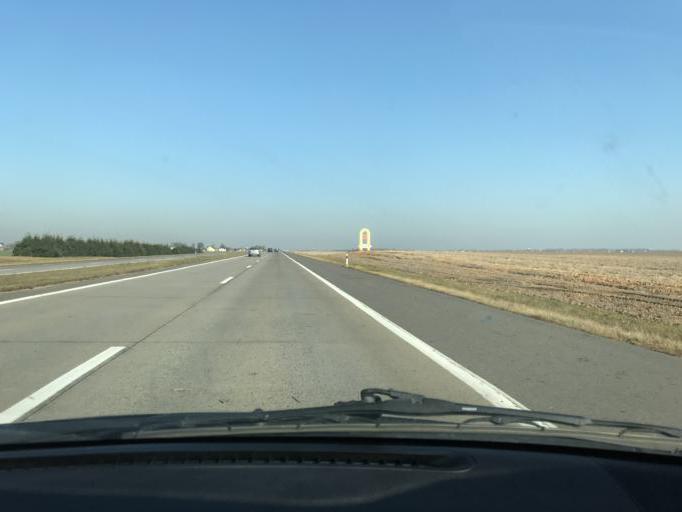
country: BY
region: Minsk
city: Samakhvalavichy
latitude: 53.6665
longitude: 27.4884
